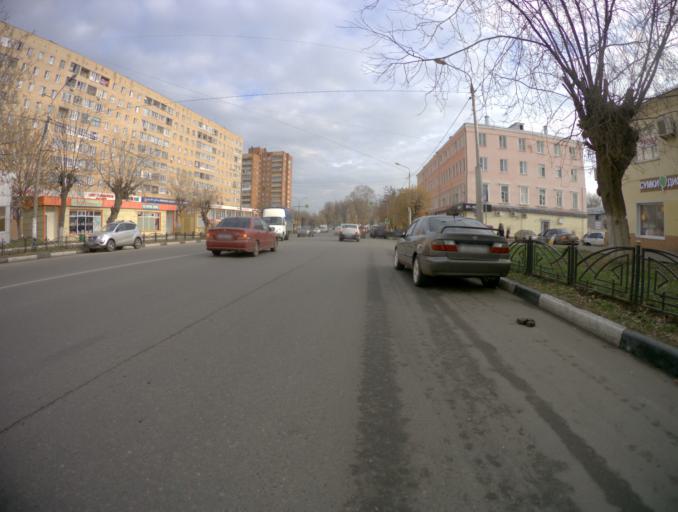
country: RU
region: Moskovskaya
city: Orekhovo-Zuyevo
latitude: 55.7985
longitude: 38.9771
